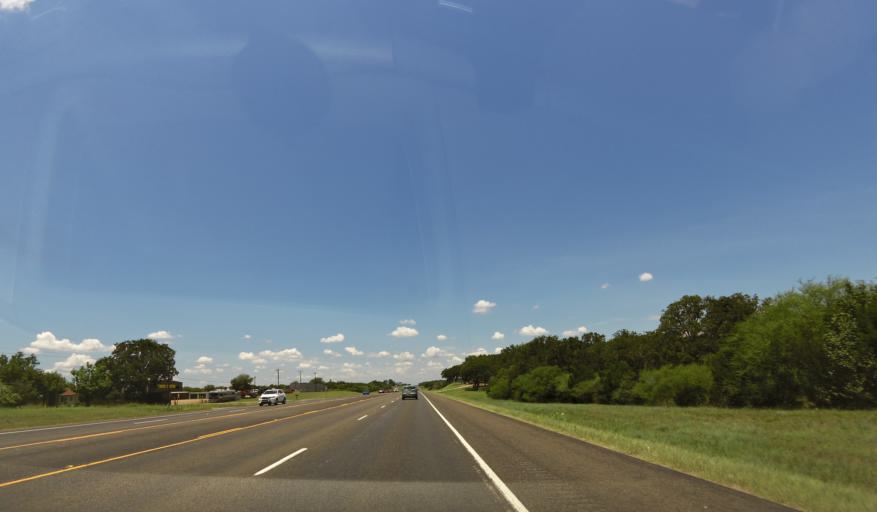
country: US
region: Texas
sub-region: Washington County
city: Brenham
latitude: 30.1724
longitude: -96.4492
